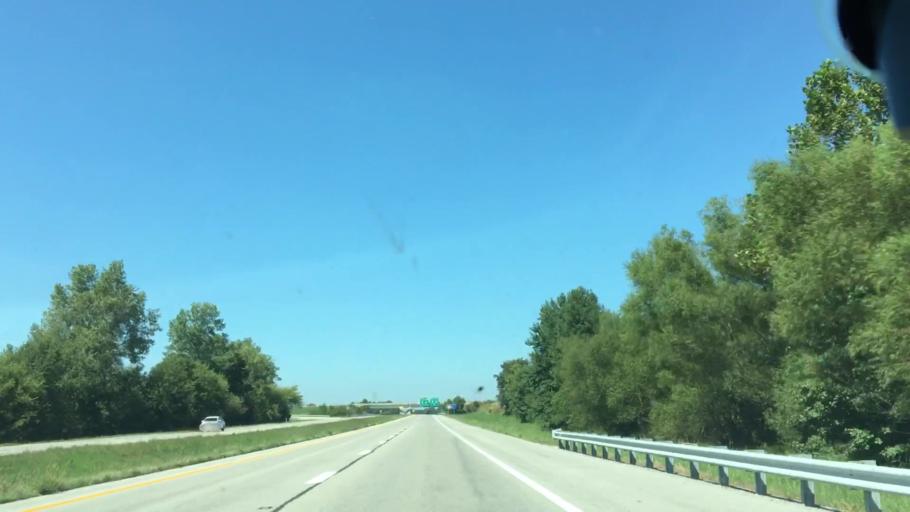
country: US
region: Kentucky
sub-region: Henderson County
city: Henderson
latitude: 37.7929
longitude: -87.5545
